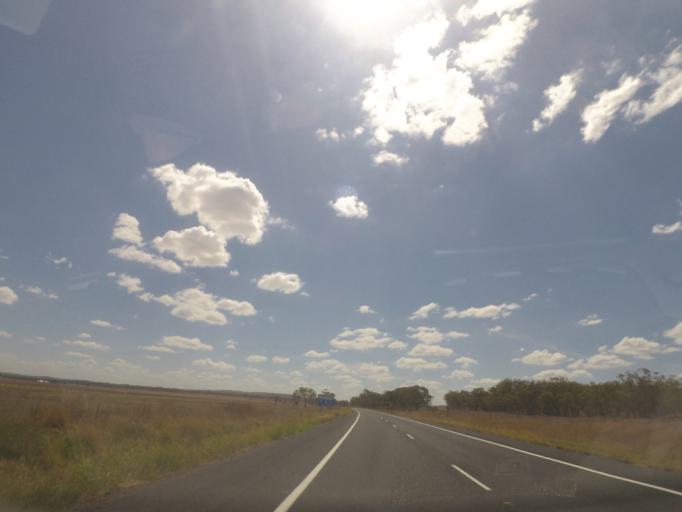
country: AU
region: Queensland
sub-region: Southern Downs
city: Warwick
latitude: -28.1789
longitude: 151.7823
